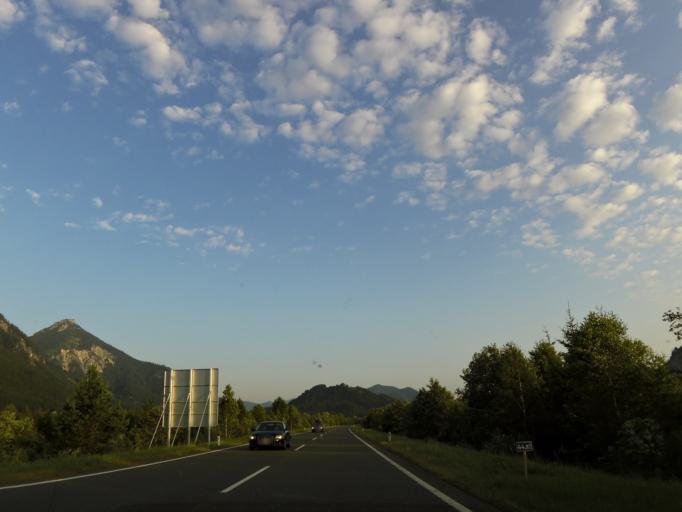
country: AT
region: Tyrol
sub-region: Politischer Bezirk Reutte
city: Musau
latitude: 47.5297
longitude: 10.6874
